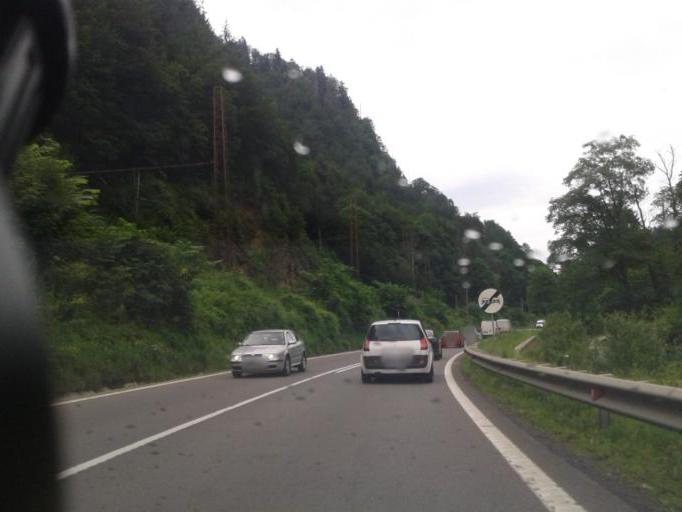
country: RO
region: Brasov
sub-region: Oras Predeal
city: Predeal
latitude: 45.5610
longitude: 25.5993
